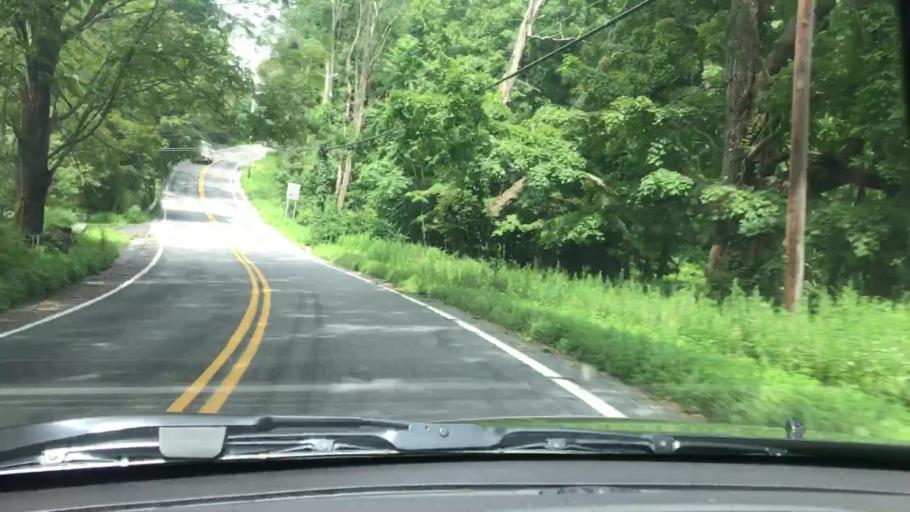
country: US
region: New York
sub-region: Westchester County
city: Bedford
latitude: 41.1774
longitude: -73.6107
